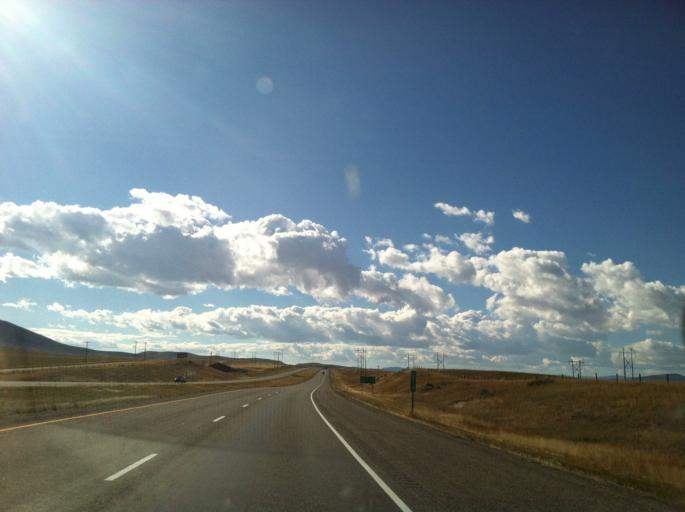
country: US
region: Montana
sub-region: Gallatin County
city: Three Forks
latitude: 45.9185
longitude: -111.6147
